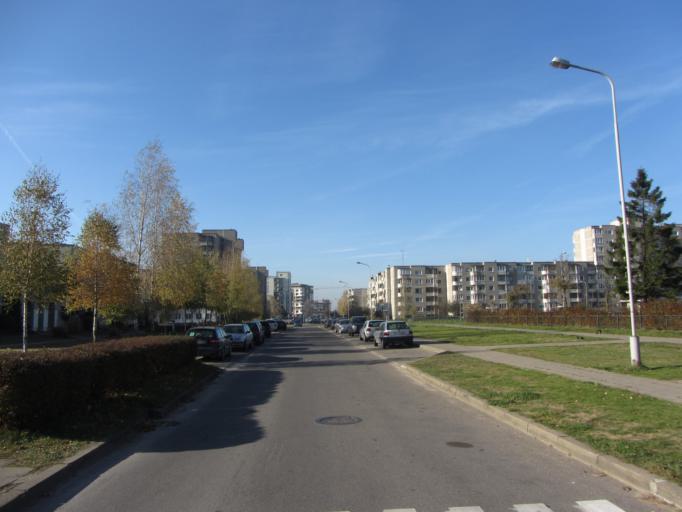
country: LT
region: Vilnius County
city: Pilaite
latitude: 54.7045
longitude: 25.1812
